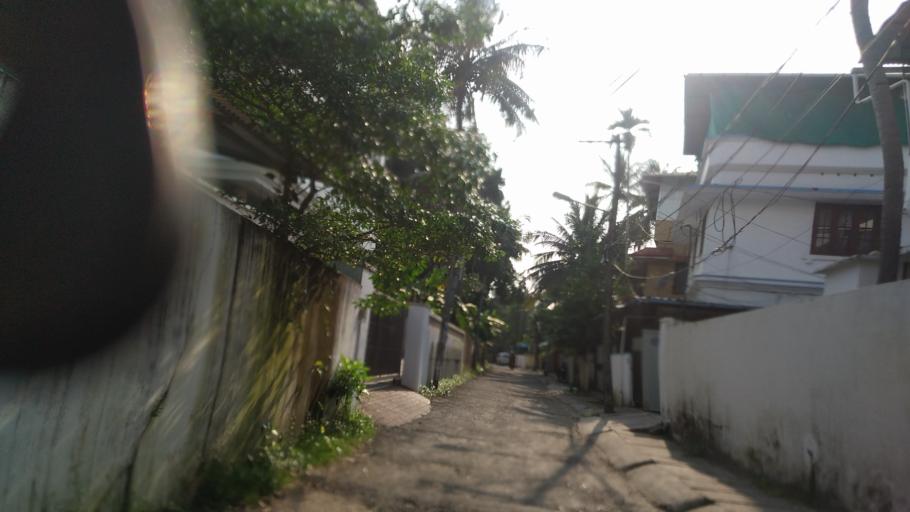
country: IN
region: Kerala
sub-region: Ernakulam
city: Elur
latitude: 9.9998
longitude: 76.2952
